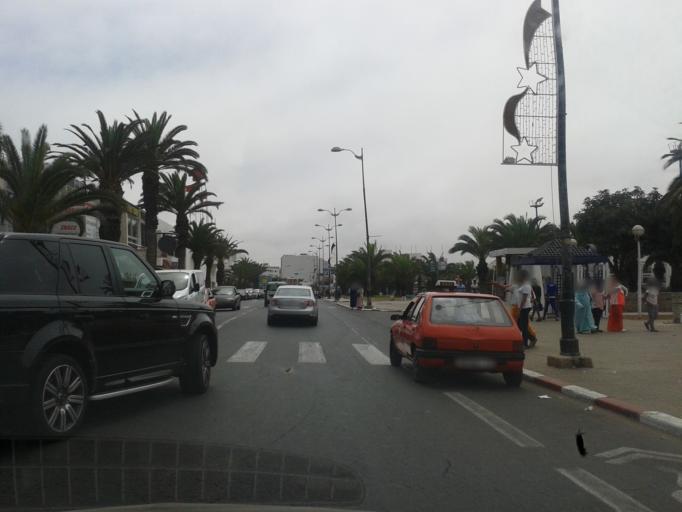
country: MA
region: Souss-Massa-Draa
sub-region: Agadir-Ida-ou-Tnan
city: Agadir
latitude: 30.4212
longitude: -9.6004
